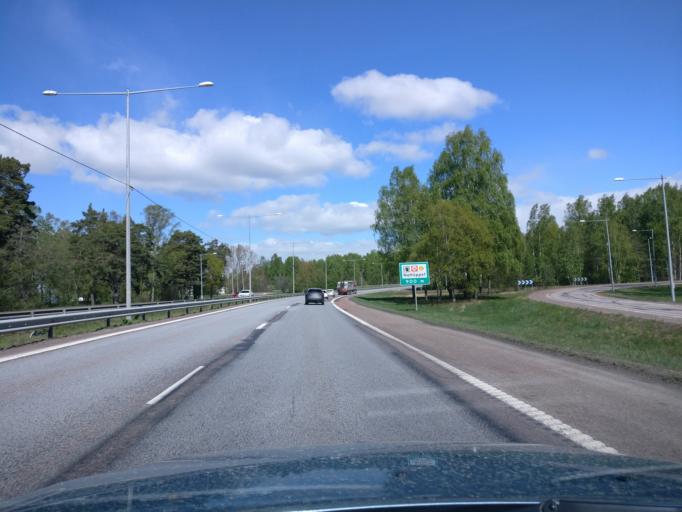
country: SE
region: Vaermland
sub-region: Karlstads Kommun
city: Karlstad
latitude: 59.3946
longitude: 13.4971
